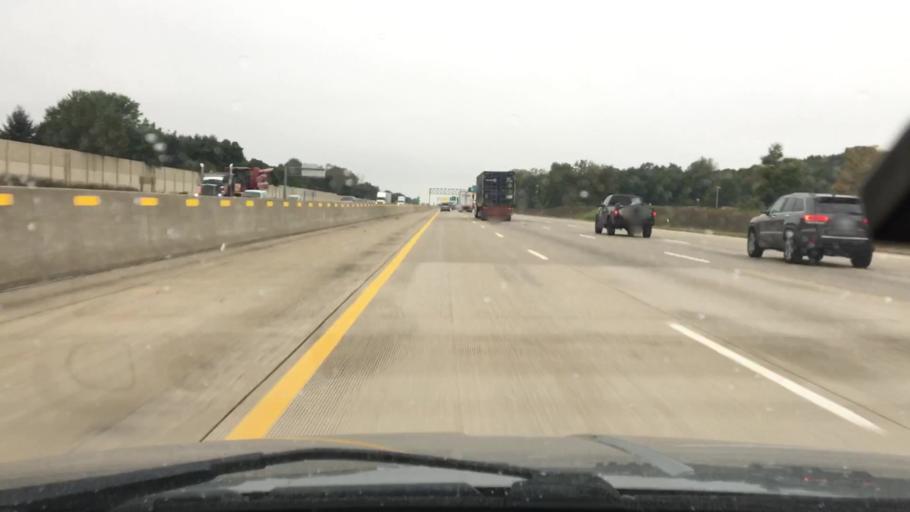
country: US
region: Michigan
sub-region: Kalamazoo County
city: Portage
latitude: 42.2379
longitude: -85.6204
